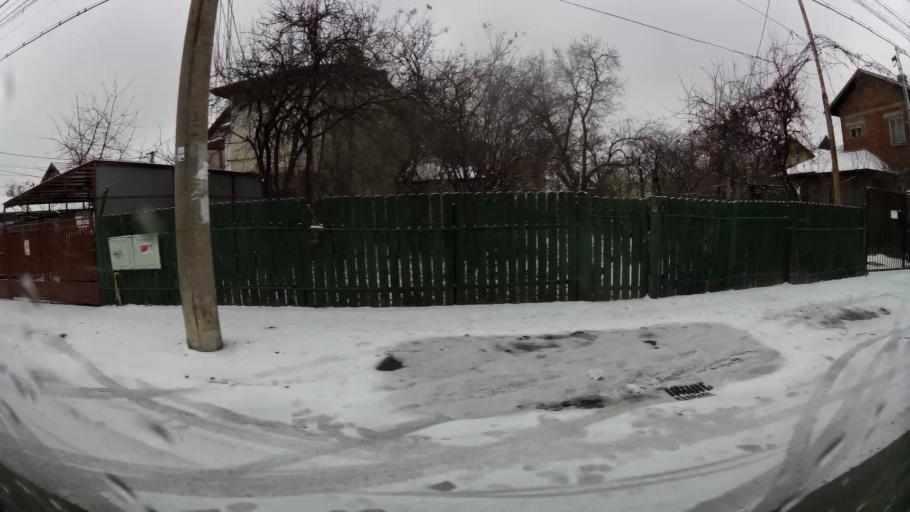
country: RO
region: Prahova
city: Ploiesti
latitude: 44.9314
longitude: 26.0220
